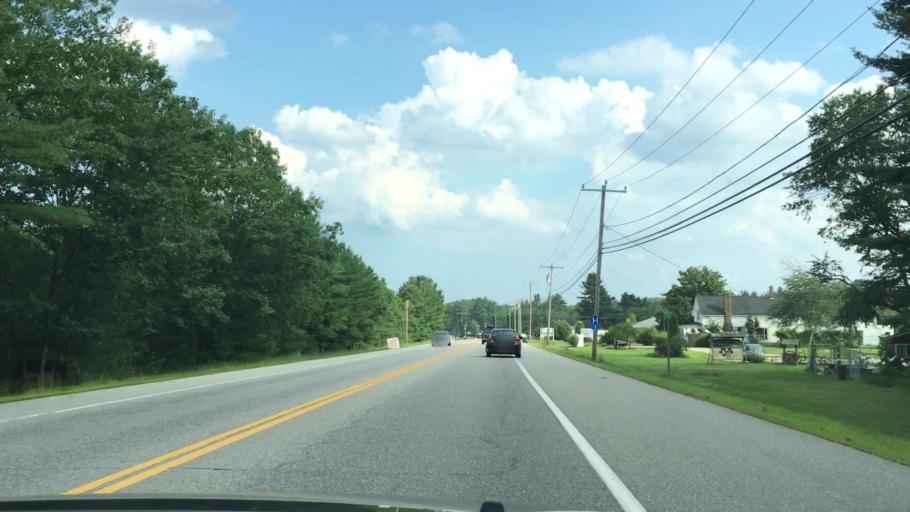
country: US
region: New Hampshire
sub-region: Strafford County
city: Rochester
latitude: 43.3451
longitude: -71.0221
